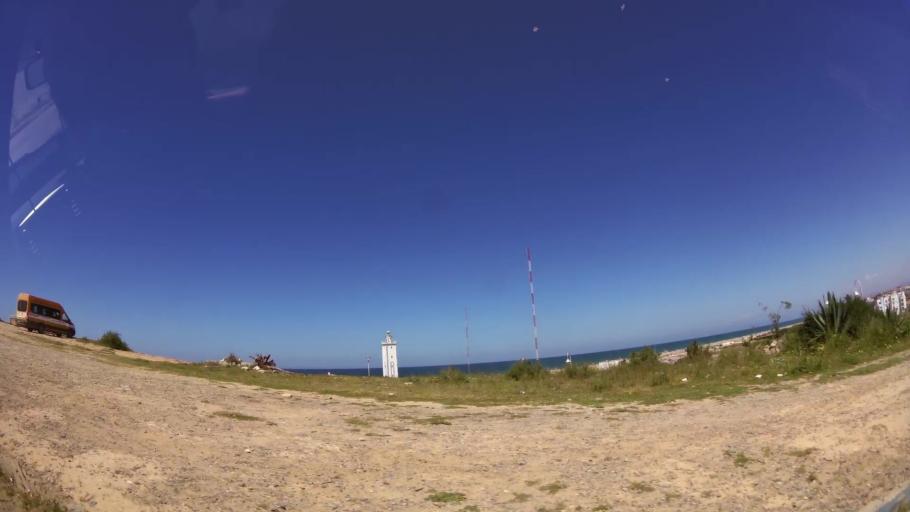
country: MA
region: Oriental
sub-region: Berkane-Taourirt
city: Madagh
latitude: 35.1401
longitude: -2.4246
